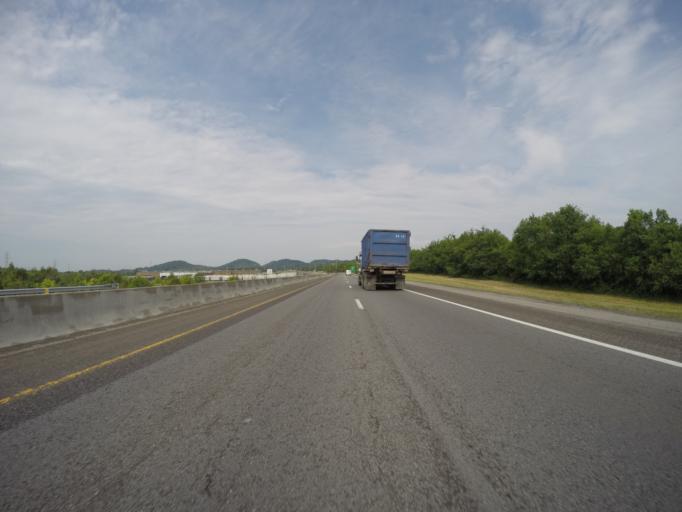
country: US
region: Tennessee
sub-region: Davidson County
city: Nashville
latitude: 36.2346
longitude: -86.8054
